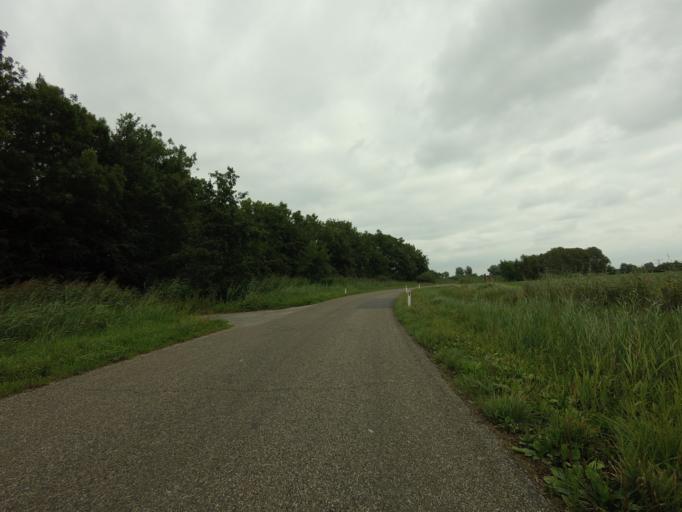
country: NL
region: Utrecht
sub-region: Stichtse Vecht
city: Breukelen
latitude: 52.2075
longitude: 4.9646
